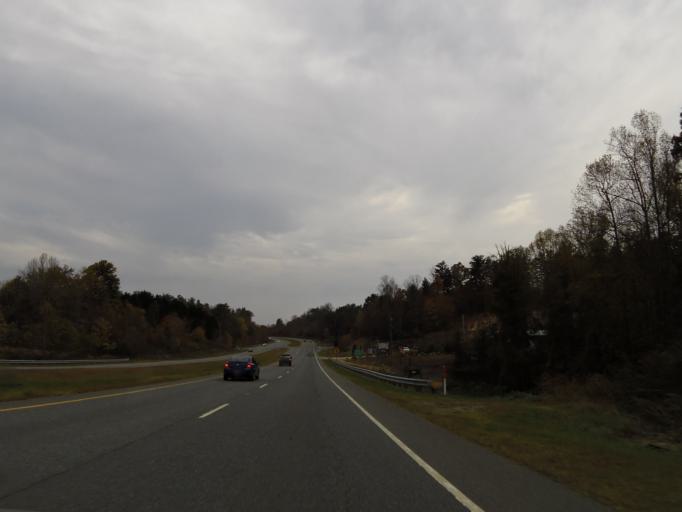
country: US
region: North Carolina
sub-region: Caldwell County
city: Lenoir
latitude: 35.9960
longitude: -81.5711
